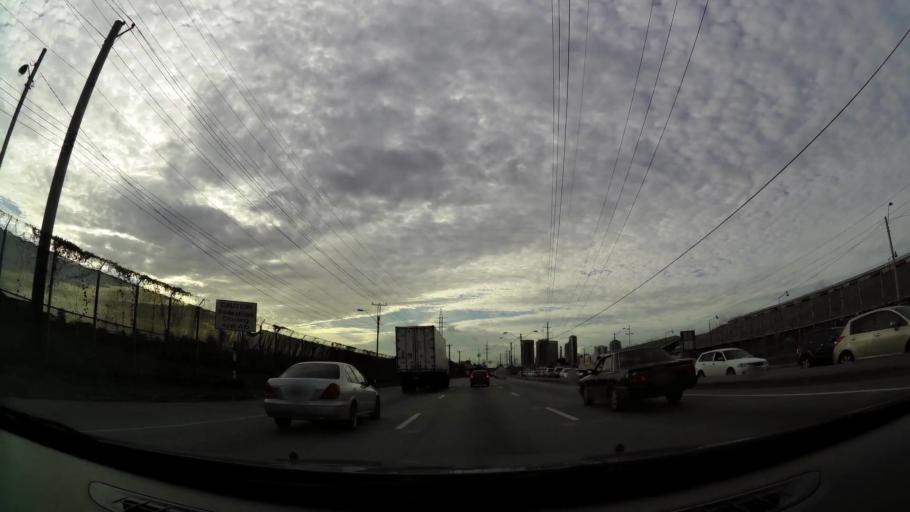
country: TT
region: San Juan/Laventille
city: Laventille
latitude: 10.6450
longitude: -61.5016
